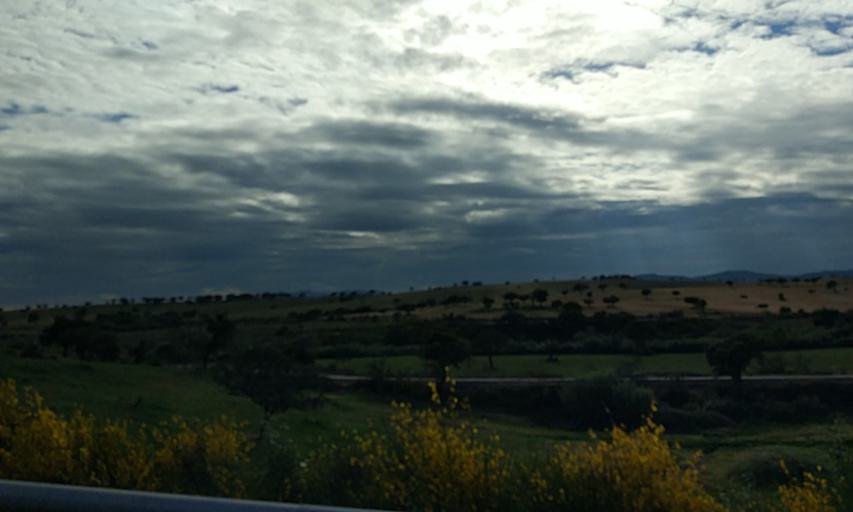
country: ES
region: Extremadura
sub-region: Provincia de Caceres
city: Moraleja
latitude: 40.1022
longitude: -6.6770
